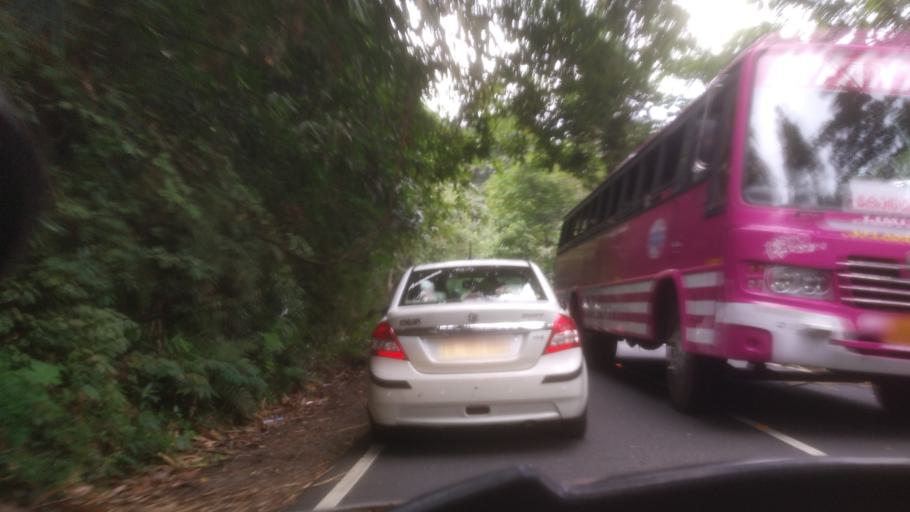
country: IN
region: Kerala
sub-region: Idukki
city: Kuttampuzha
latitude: 10.0626
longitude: 76.8025
